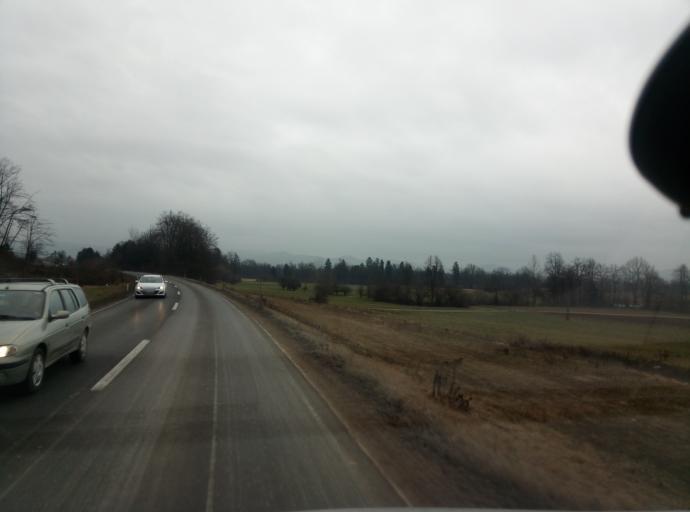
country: SI
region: Dol pri Ljubljani
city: Dol pri Ljubljani
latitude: 46.0929
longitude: 14.5637
